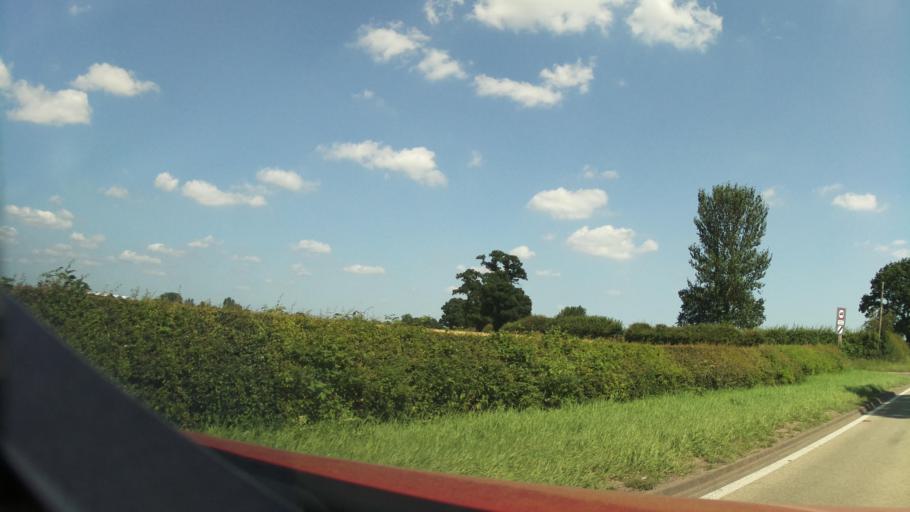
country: GB
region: England
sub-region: Warwickshire
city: Hartshill
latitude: 52.5655
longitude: -1.5063
